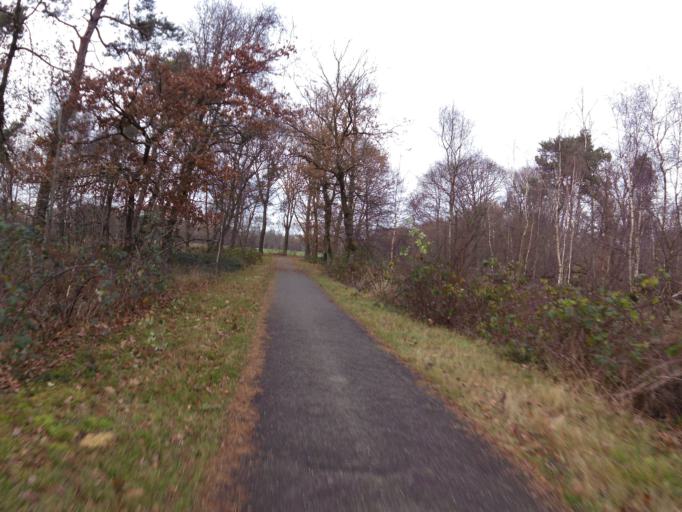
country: NL
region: North Brabant
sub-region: Gemeente Oss
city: Berghem
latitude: 51.7270
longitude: 5.5791
